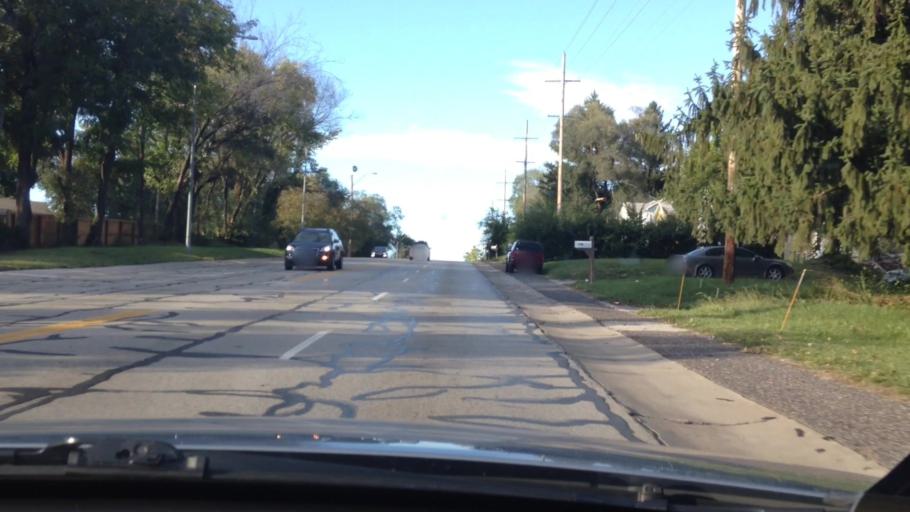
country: US
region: Missouri
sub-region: Platte County
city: Riverside
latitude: 39.1745
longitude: -94.5767
